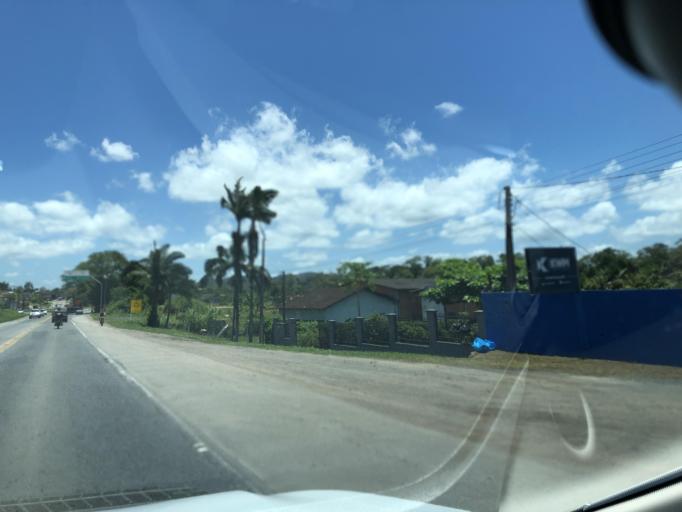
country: BR
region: Santa Catarina
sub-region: Joinville
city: Joinville
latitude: -26.4175
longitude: -48.7758
